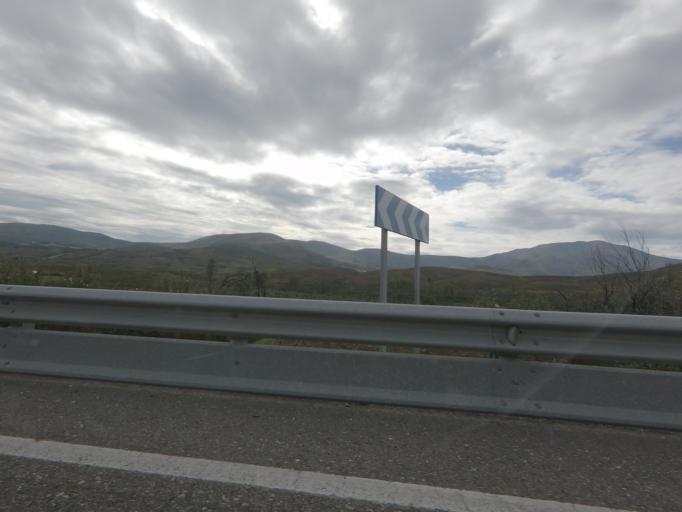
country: ES
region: Extremadura
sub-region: Provincia de Caceres
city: Acebo
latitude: 40.1976
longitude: -6.6761
